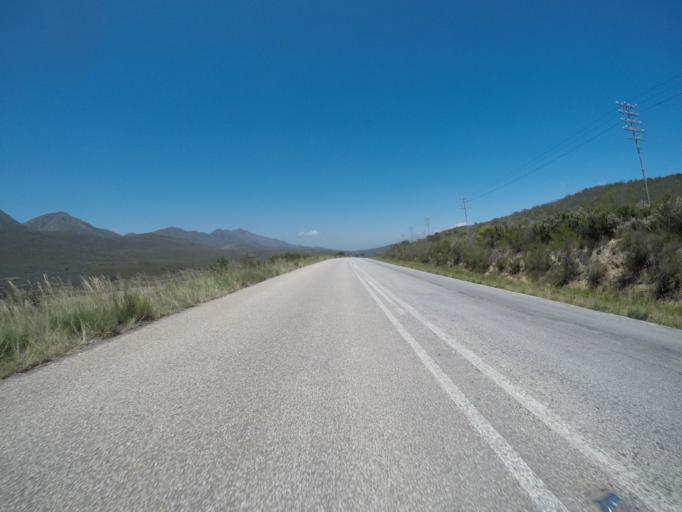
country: ZA
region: Eastern Cape
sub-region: Cacadu District Municipality
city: Kareedouw
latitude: -33.8946
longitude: 24.1097
